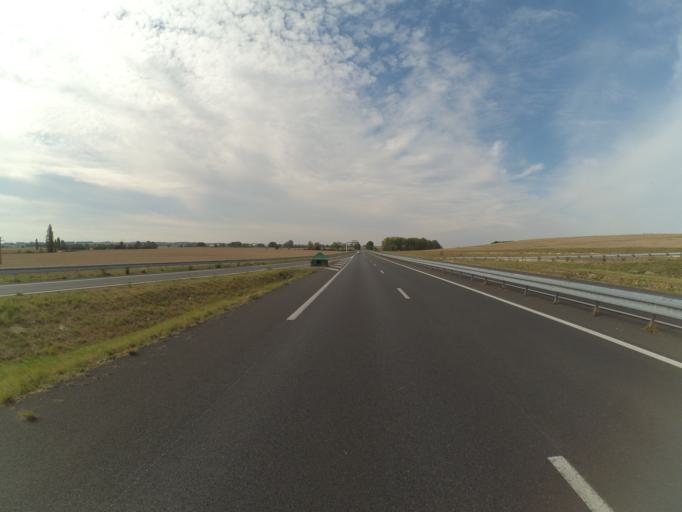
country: FR
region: Pays de la Loire
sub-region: Departement de Maine-et-Loire
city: Doue-la-Fontaine
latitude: 47.2001
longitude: -0.2208
